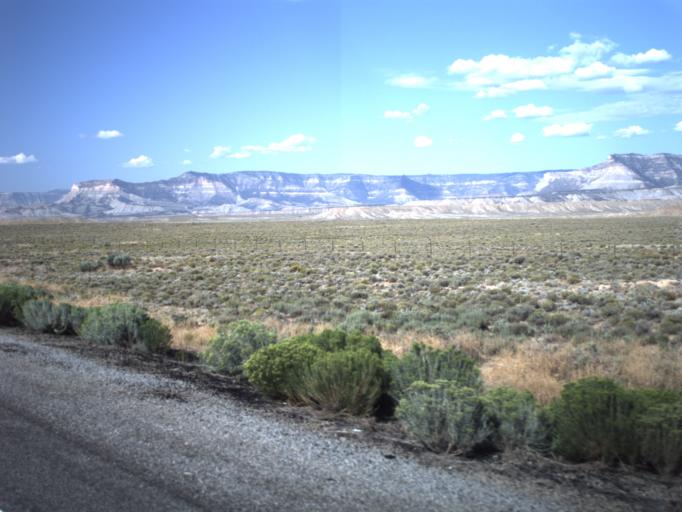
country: US
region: Utah
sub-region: Emery County
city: Huntington
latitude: 39.3990
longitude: -110.8923
